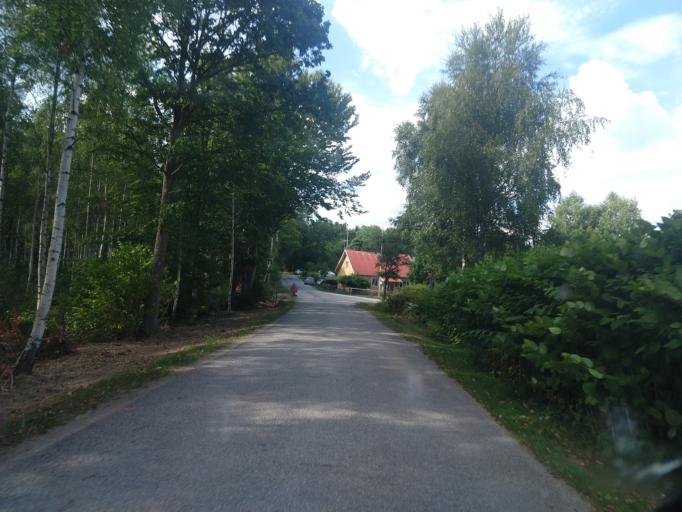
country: SE
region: Blekinge
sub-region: Karlskrona Kommun
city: Nattraby
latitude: 56.2560
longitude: 15.5243
